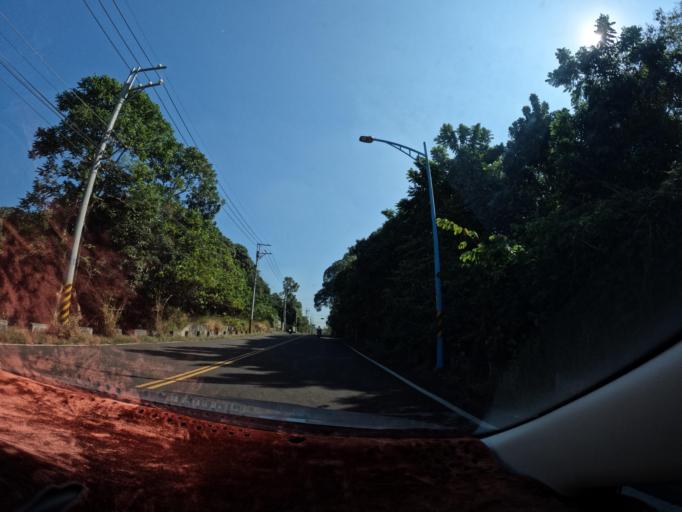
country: TW
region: Taiwan
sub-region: Tainan
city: Tainan
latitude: 23.0354
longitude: 120.3444
